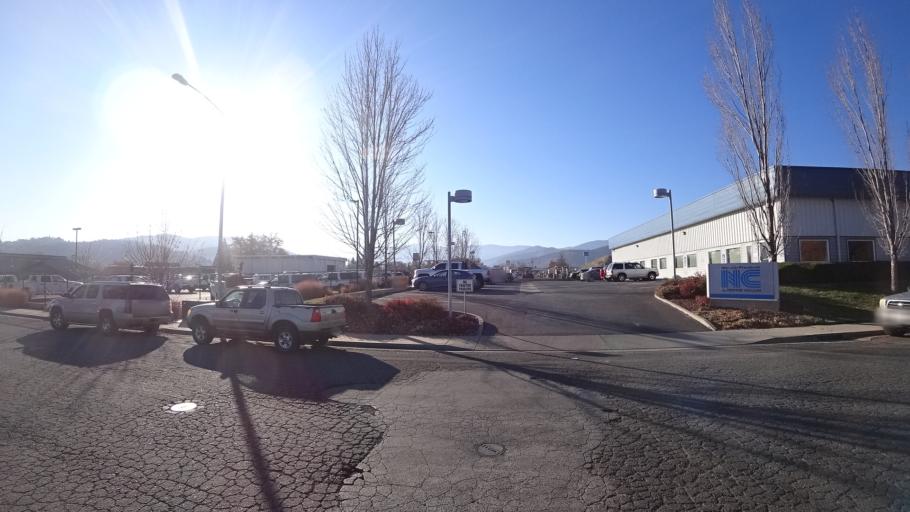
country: US
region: California
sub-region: Siskiyou County
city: Yreka
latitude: 41.7071
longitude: -122.6457
